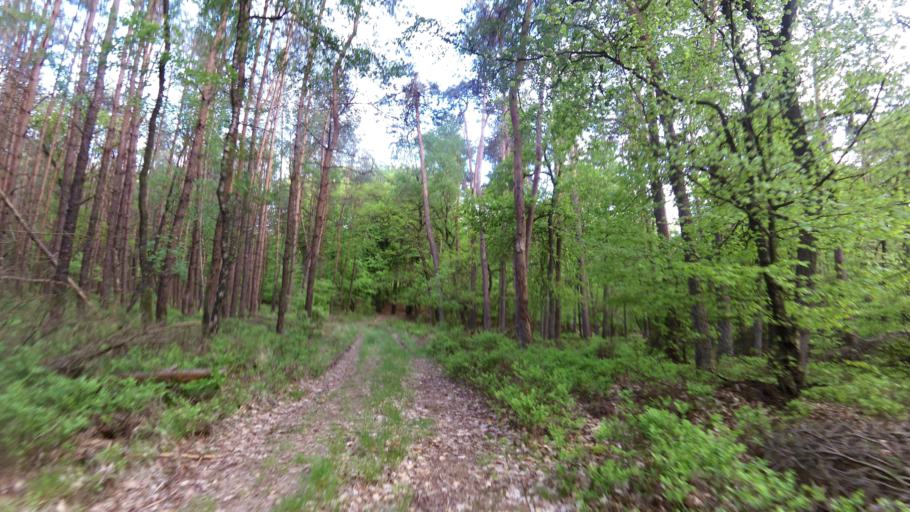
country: NL
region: Gelderland
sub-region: Gemeente Rozendaal
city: Rozendaal
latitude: 52.0262
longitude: 5.9563
